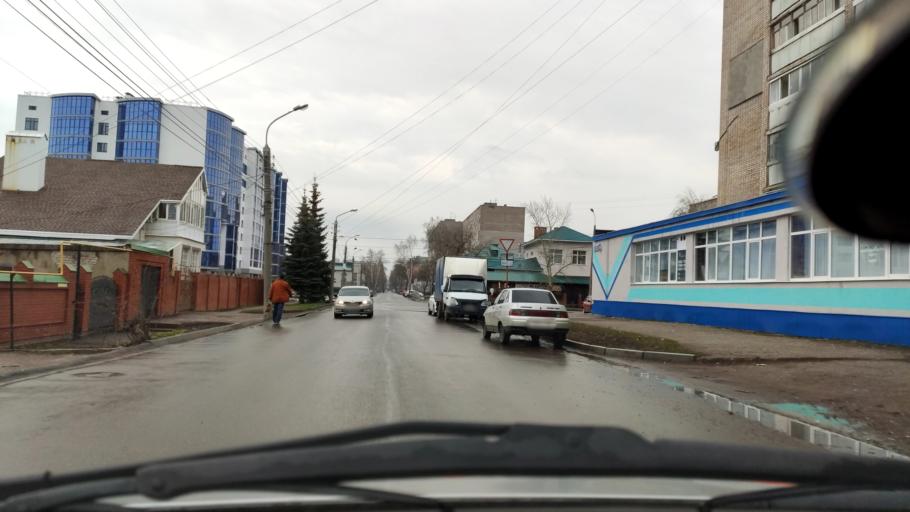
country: RU
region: Bashkortostan
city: Sterlitamak
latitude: 53.6233
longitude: 55.9585
